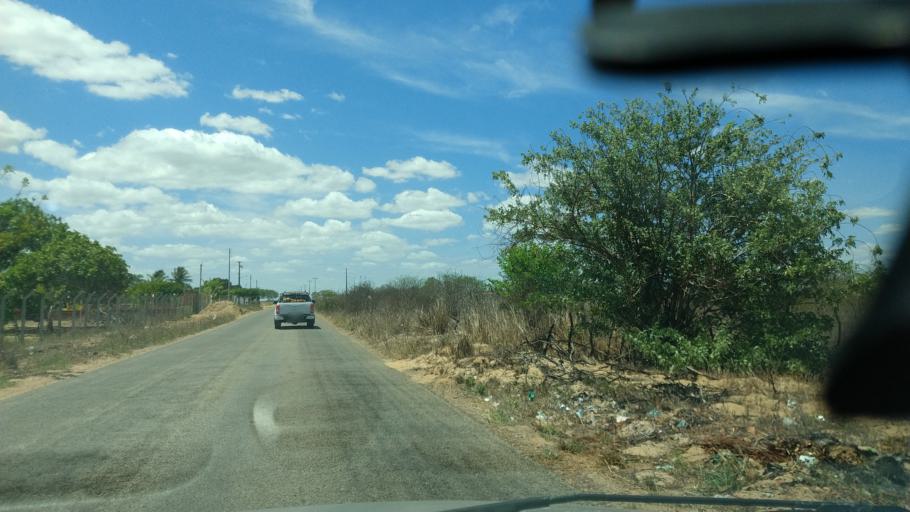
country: BR
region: Rio Grande do Norte
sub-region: Sao Paulo Do Potengi
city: Sao Paulo do Potengi
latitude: -5.9150
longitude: -35.7373
